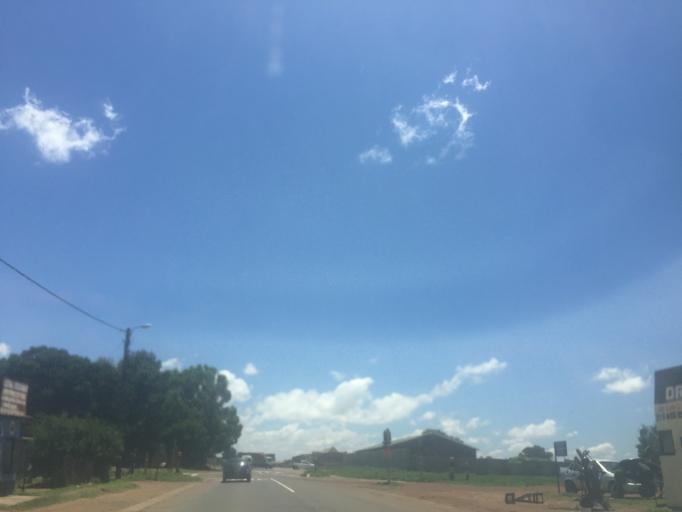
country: ZA
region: Mpumalanga
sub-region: Nkangala District Municipality
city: Delmas
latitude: -26.1324
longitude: 28.6903
